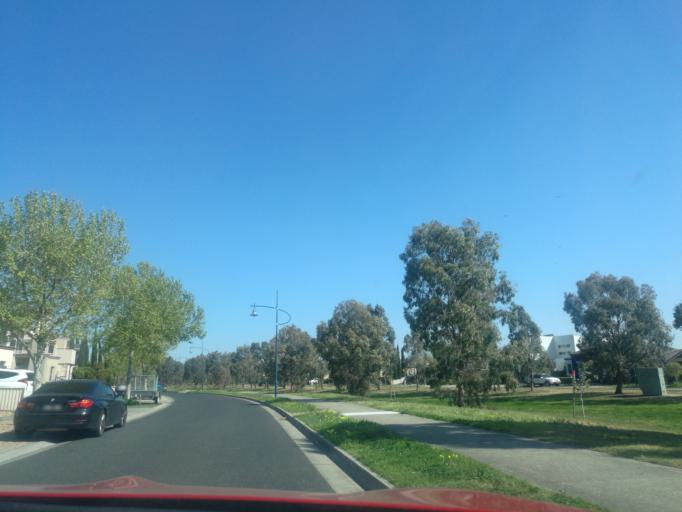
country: AU
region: Victoria
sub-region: Wyndham
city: Point Cook
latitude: -37.8951
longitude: 144.7396
